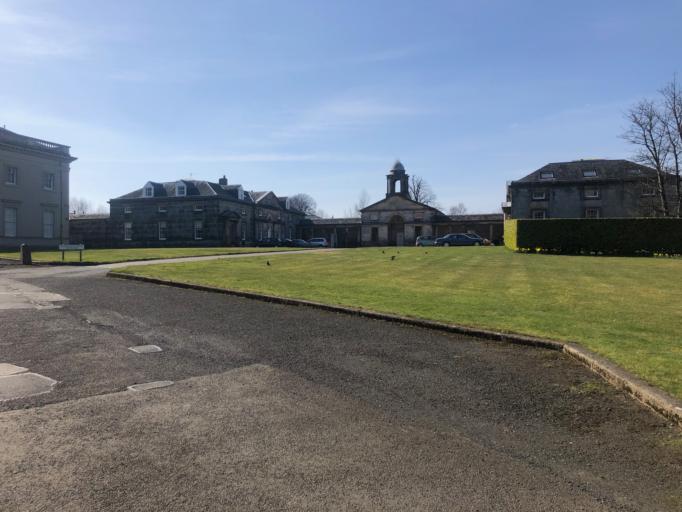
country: GB
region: Scotland
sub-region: West Lothian
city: Seafield
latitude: 55.9397
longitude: -3.1363
